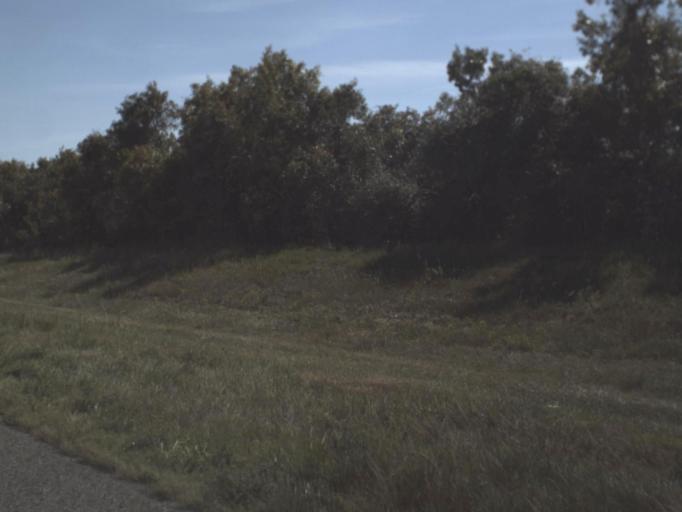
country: US
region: Florida
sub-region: Highlands County
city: Lake Placid
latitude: 27.2747
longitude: -81.3520
